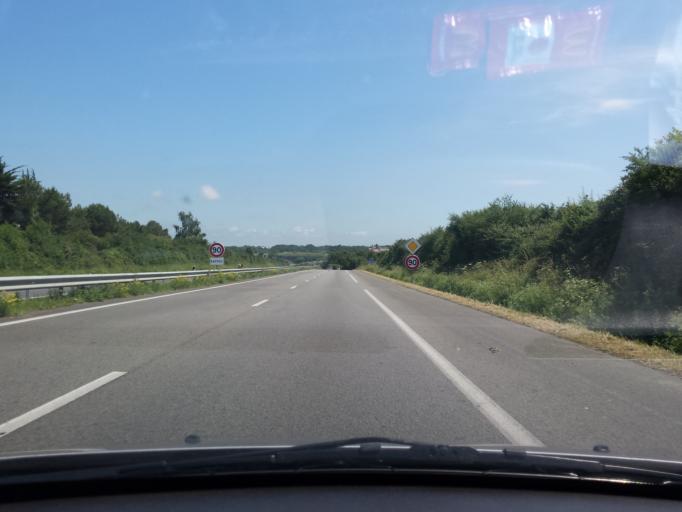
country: FR
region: Pays de la Loire
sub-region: Departement de la Loire-Atlantique
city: Pornic
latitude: 47.1211
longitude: -2.0953
